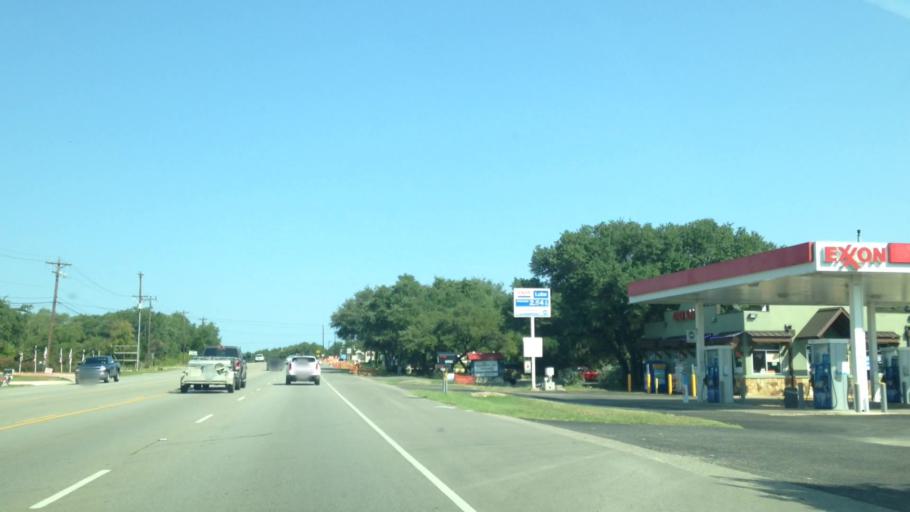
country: US
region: Texas
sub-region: Williamson County
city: Serenada
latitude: 30.6694
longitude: -97.6986
